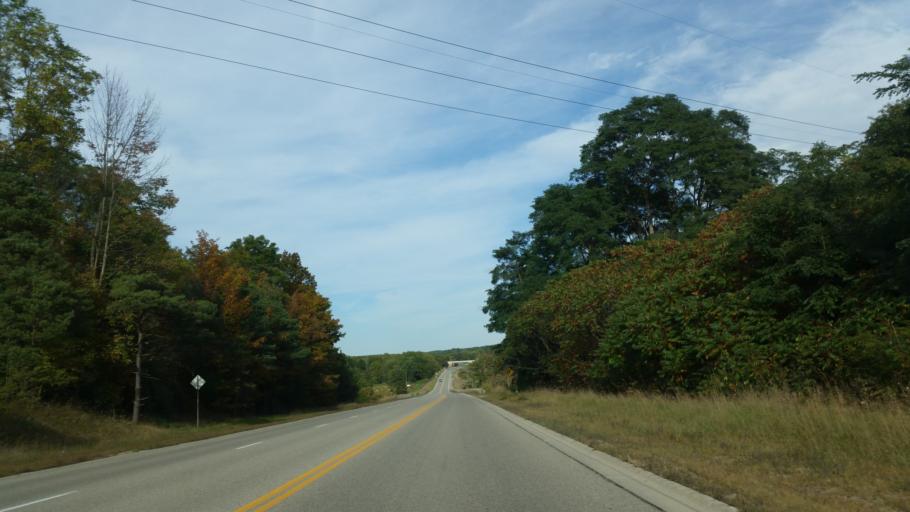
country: CA
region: Ontario
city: Delaware
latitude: 42.8929
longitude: -81.4417
